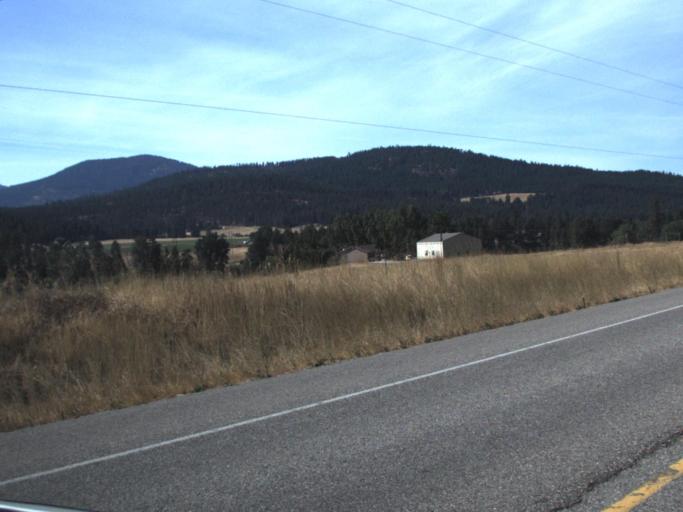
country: US
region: Washington
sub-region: Stevens County
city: Chewelah
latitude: 48.3129
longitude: -117.8000
